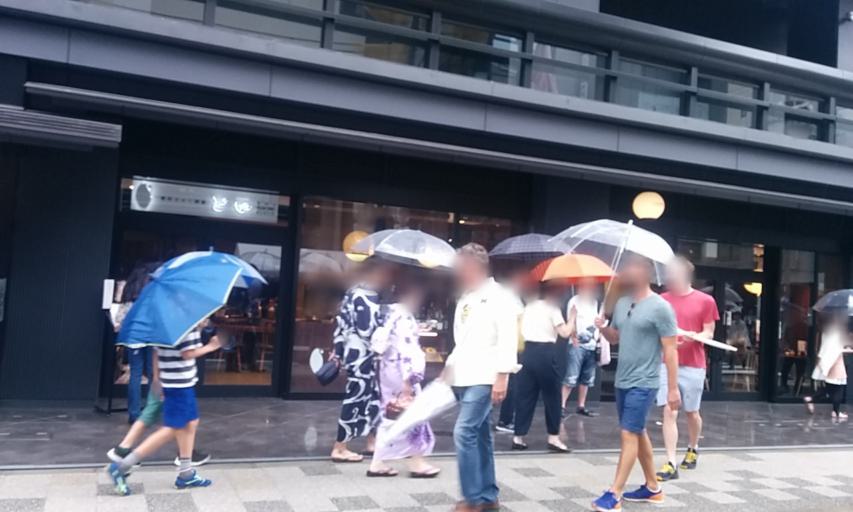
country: JP
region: Kyoto
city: Kyoto
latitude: 35.0027
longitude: 135.7582
